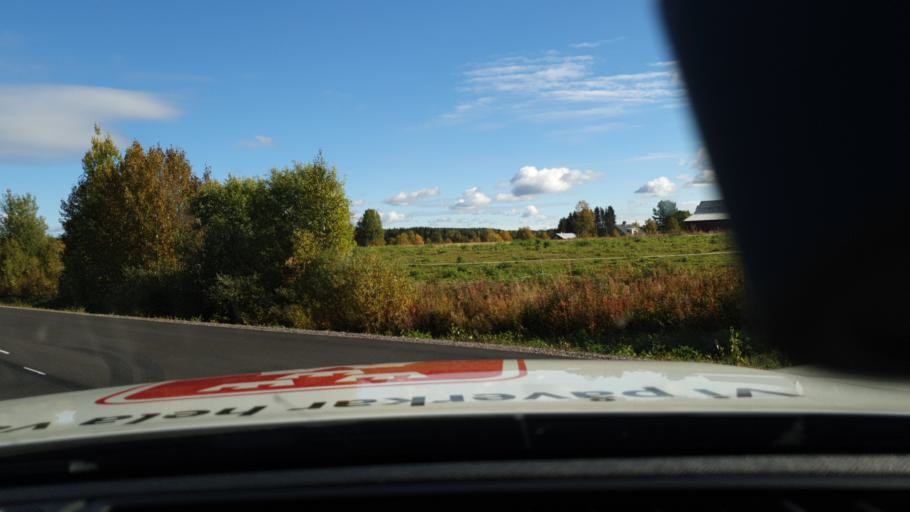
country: SE
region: Norrbotten
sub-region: Pajala Kommun
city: Pajala
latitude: 67.2056
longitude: 23.3933
